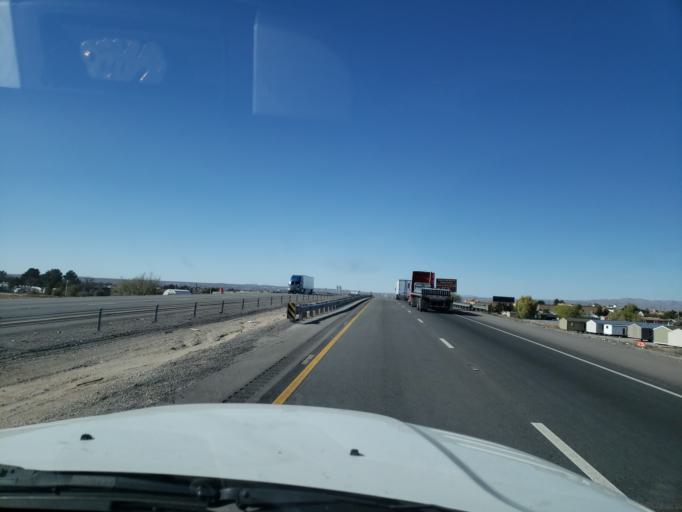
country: US
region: New Mexico
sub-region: Dona Ana County
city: Mesilla
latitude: 32.2853
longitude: -106.7809
